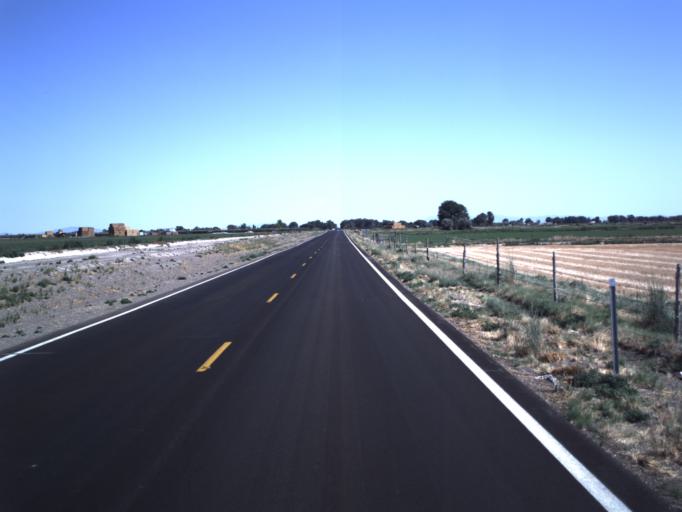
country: US
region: Utah
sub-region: Millard County
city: Delta
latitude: 39.2678
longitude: -112.6531
